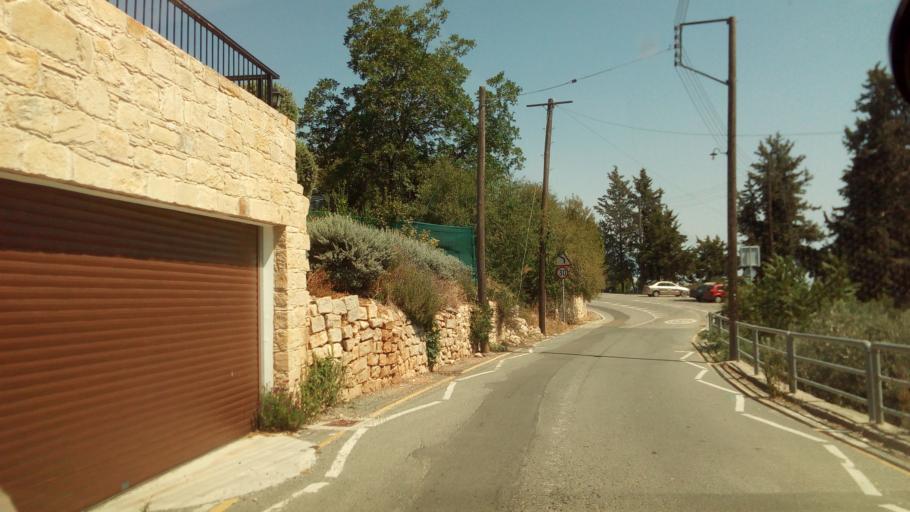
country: CY
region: Limassol
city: Pachna
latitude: 34.8246
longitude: 32.8358
